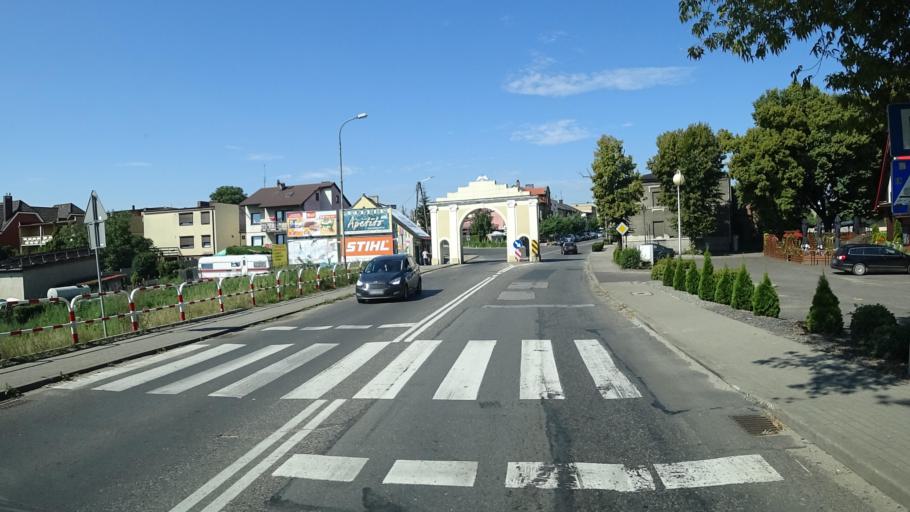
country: PL
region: Greater Poland Voivodeship
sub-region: Powiat koninski
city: Slesin
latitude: 52.3702
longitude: 18.3097
